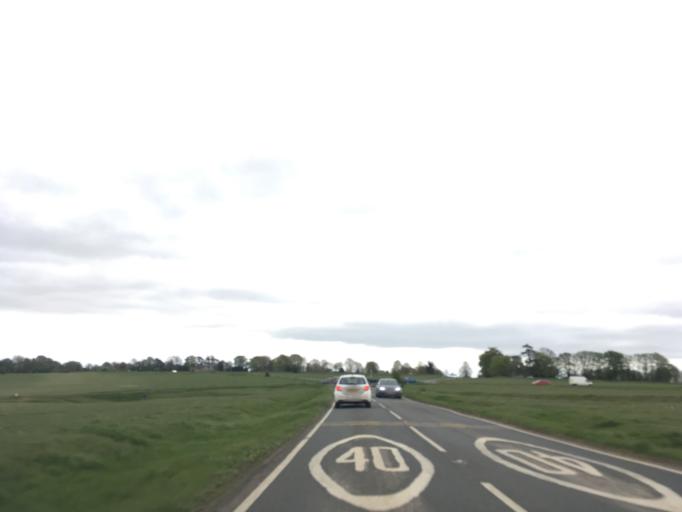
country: GB
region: England
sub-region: Gloucestershire
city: Nailsworth
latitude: 51.7110
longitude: -2.2079
